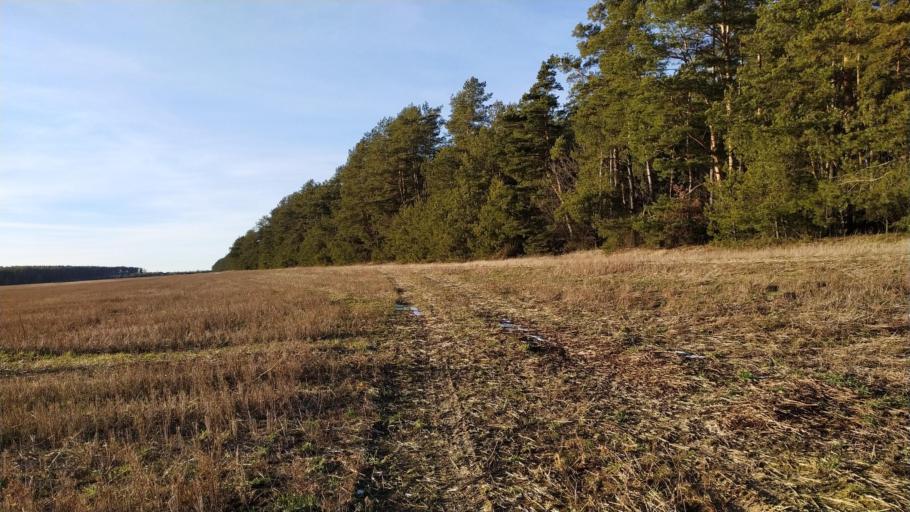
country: BY
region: Brest
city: Kamyanyets
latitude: 52.3687
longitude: 23.8637
